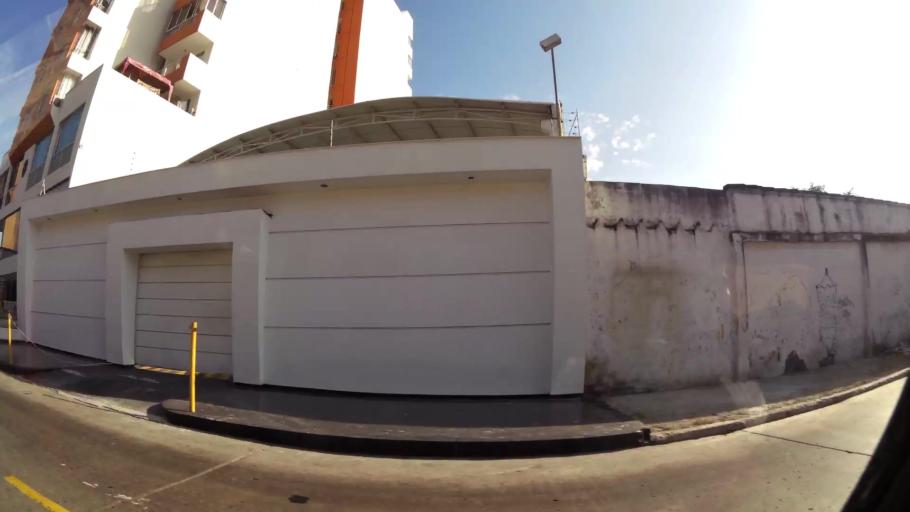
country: CO
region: Atlantico
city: Barranquilla
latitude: 10.9970
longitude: -74.8033
